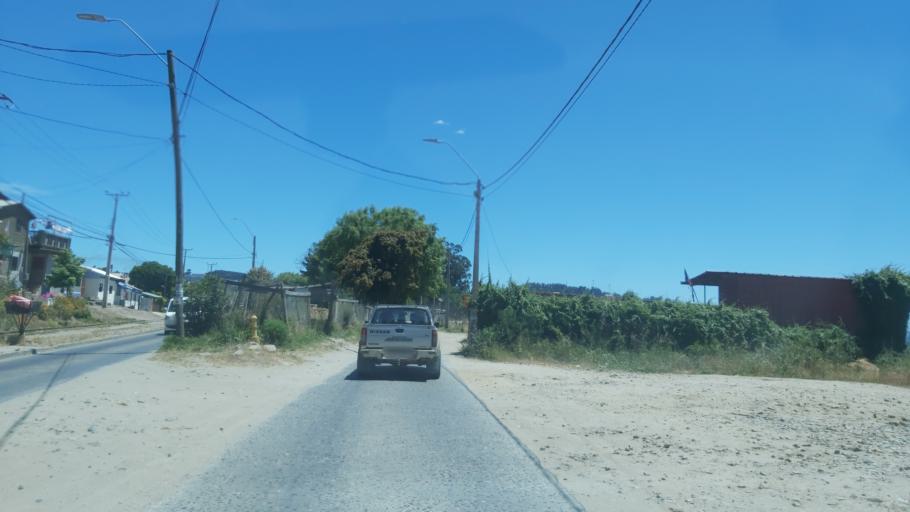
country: CL
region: Maule
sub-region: Provincia de Talca
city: Constitucion
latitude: -35.3400
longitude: -72.3973
